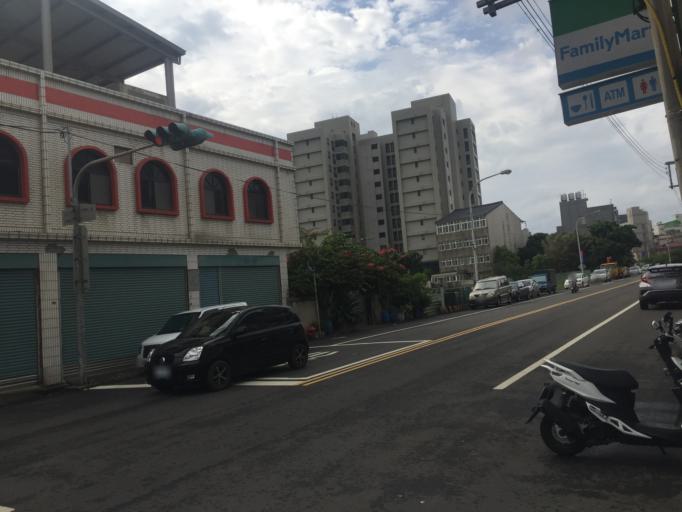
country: TW
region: Taiwan
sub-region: Hsinchu
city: Hsinchu
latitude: 24.6973
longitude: 120.8934
